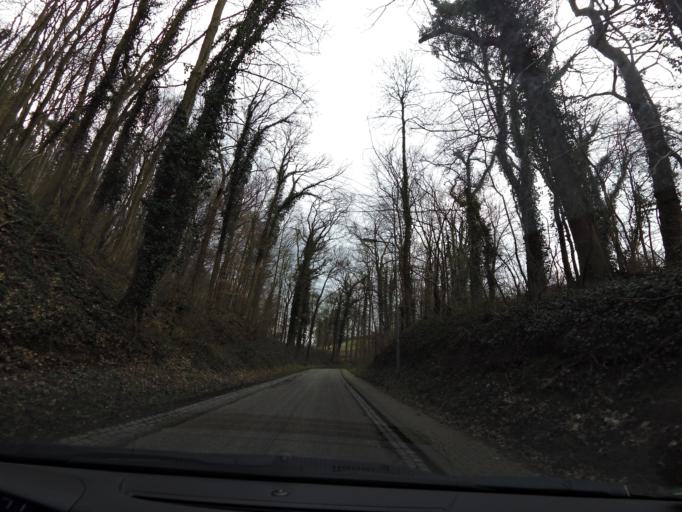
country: NL
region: Limburg
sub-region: Valkenburg aan de Geul
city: Sibbe
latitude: 50.8517
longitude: 5.8347
